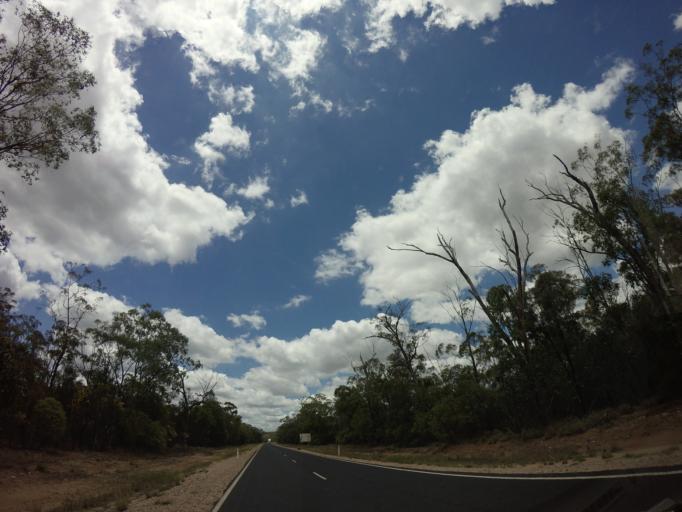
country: AU
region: Queensland
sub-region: Goondiwindi
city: Goondiwindi
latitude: -28.0410
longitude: 150.7982
